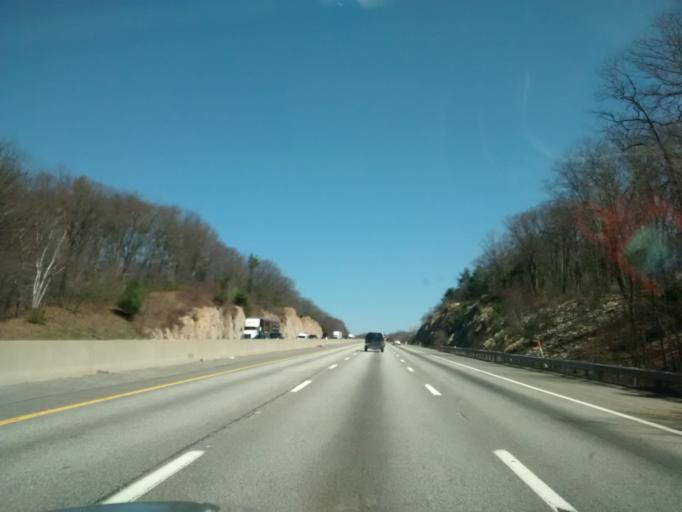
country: US
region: Massachusetts
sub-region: Worcester County
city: Grafton
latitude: 42.2277
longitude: -71.6453
